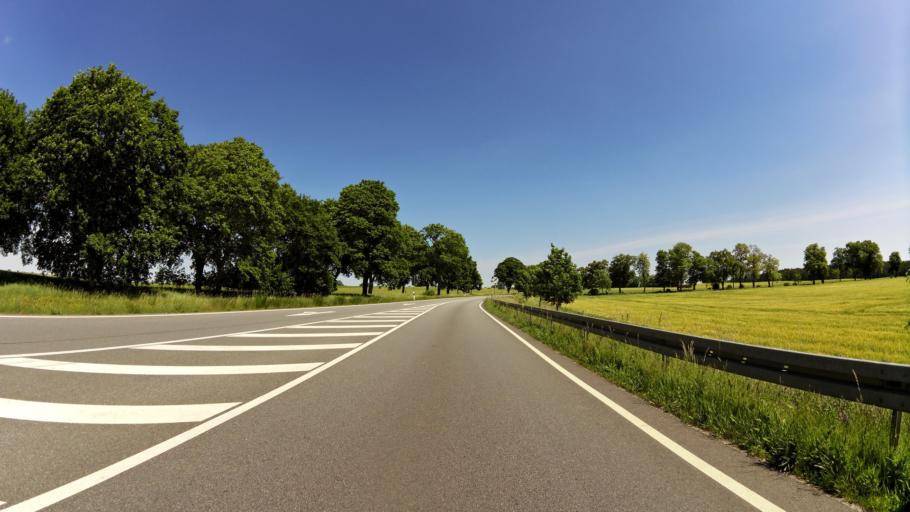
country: DE
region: Brandenburg
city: Muncheberg
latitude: 52.5036
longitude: 14.1781
